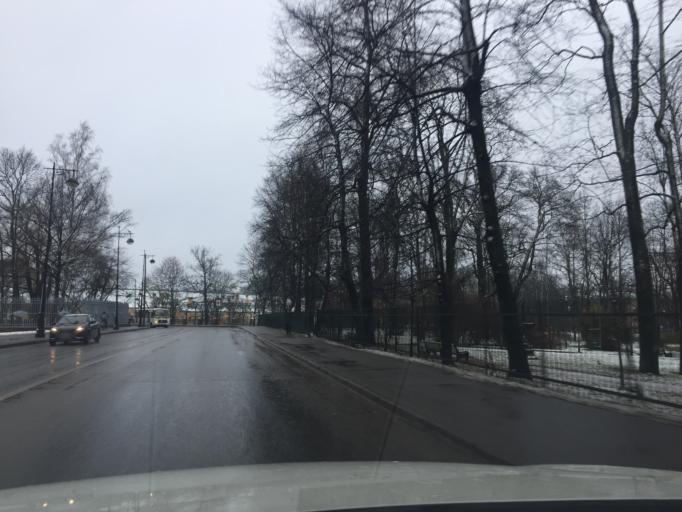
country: RU
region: St.-Petersburg
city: Pushkin
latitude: 59.7127
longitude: 30.4103
